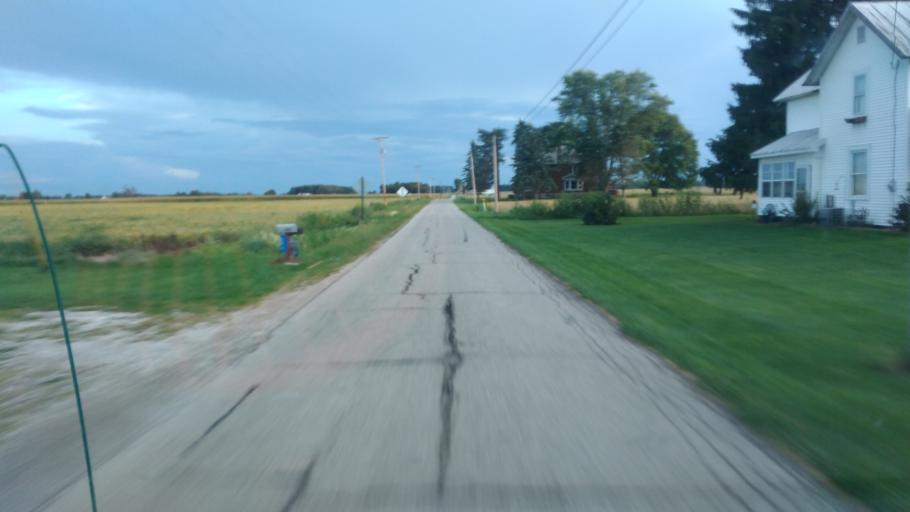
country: US
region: Ohio
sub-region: Crawford County
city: Bucyrus
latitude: 40.7184
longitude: -82.9186
